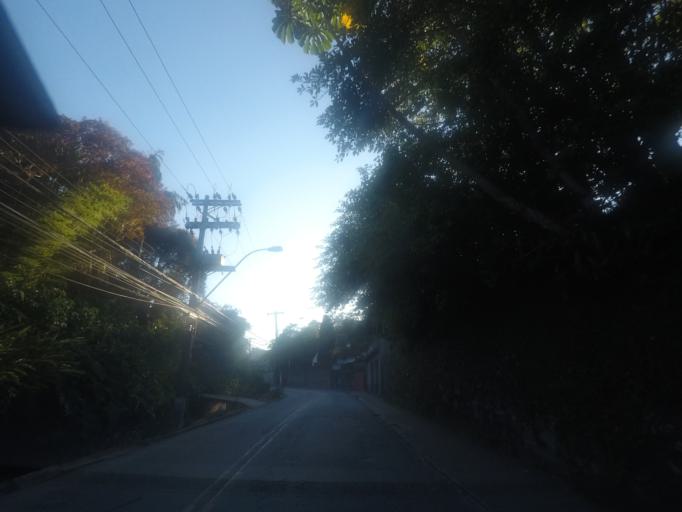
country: BR
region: Rio de Janeiro
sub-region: Petropolis
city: Petropolis
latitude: -22.5240
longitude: -43.1853
